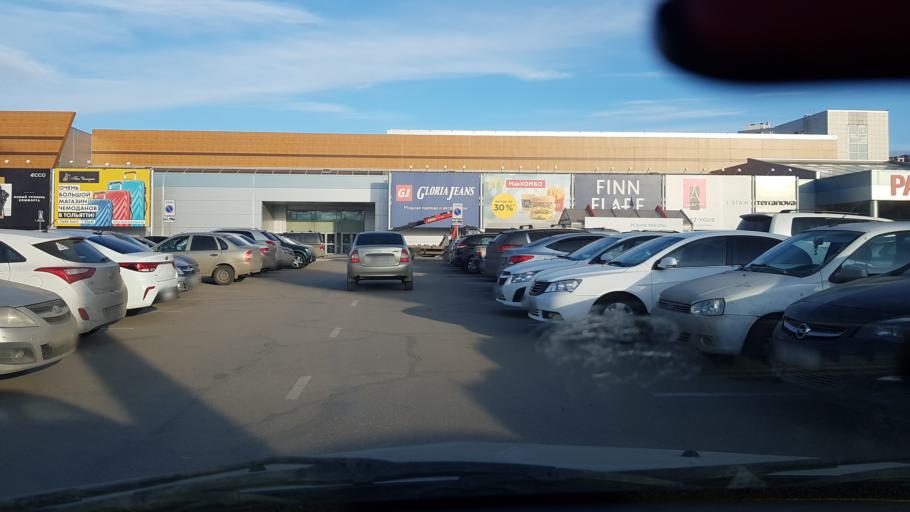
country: RU
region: Samara
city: Tol'yatti
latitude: 53.5403
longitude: 49.3898
